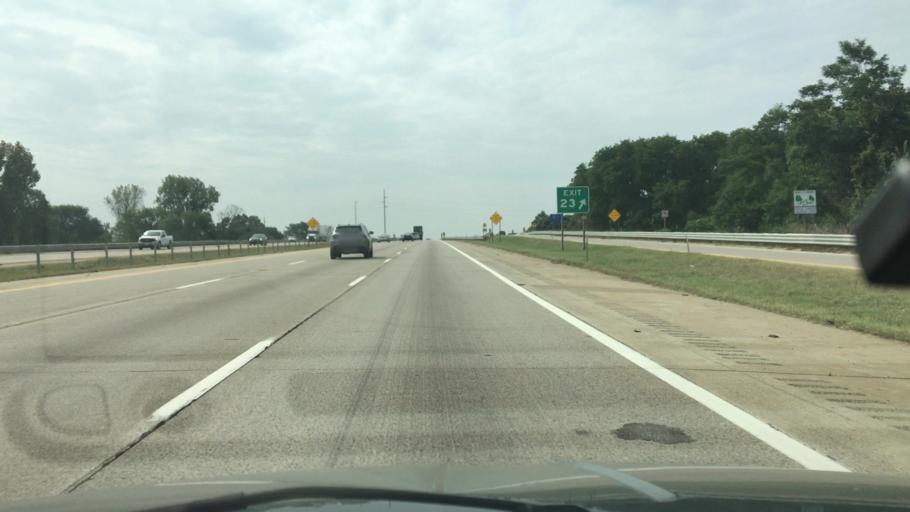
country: US
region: Michigan
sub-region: Berrien County
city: Stevensville
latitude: 42.0353
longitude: -86.5069
